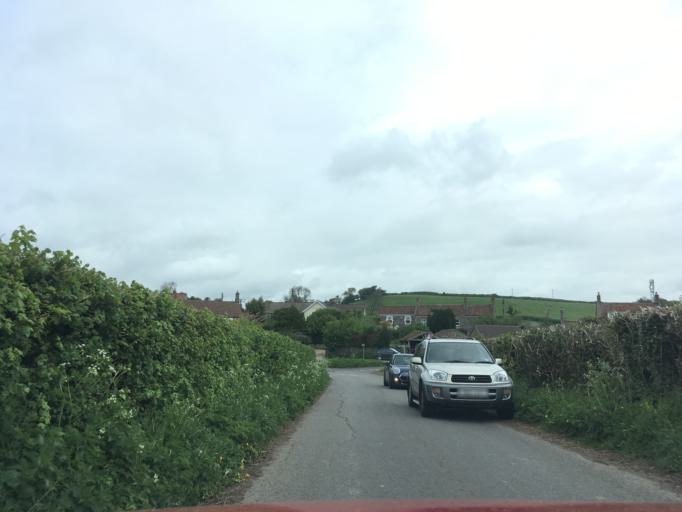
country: GB
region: England
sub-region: Bath and North East Somerset
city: Clutton
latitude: 51.3359
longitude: -2.5194
